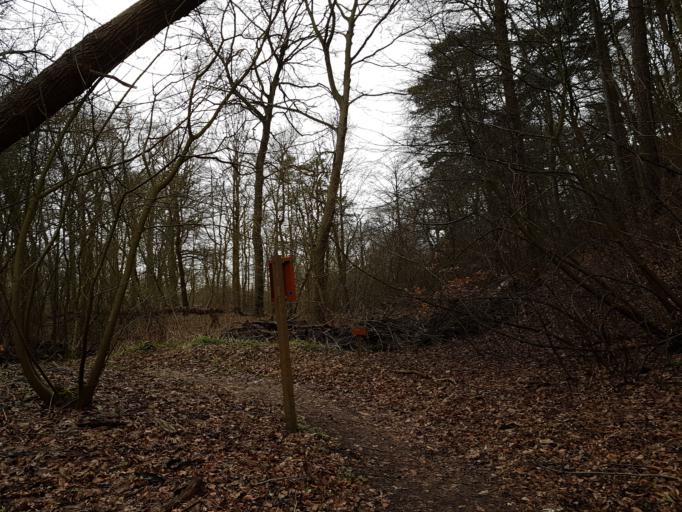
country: NL
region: North Holland
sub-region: Gemeente Bloemendaal
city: Bloemendaal
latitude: 52.3876
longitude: 4.5957
